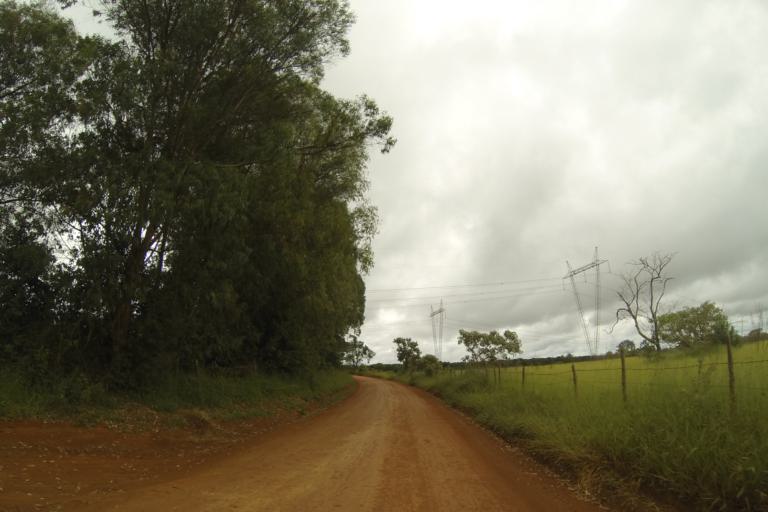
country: BR
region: Minas Gerais
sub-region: Campos Altos
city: Campos Altos
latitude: -19.8668
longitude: -46.3065
